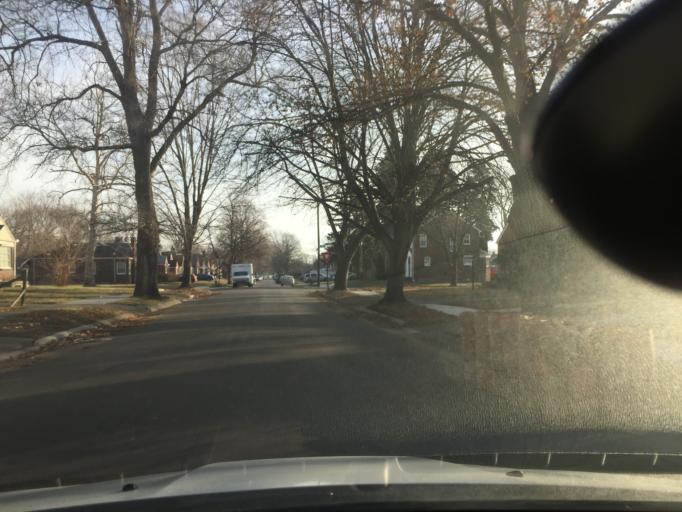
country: US
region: Michigan
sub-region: Macomb County
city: Eastpointe
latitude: 42.4339
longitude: -82.9588
